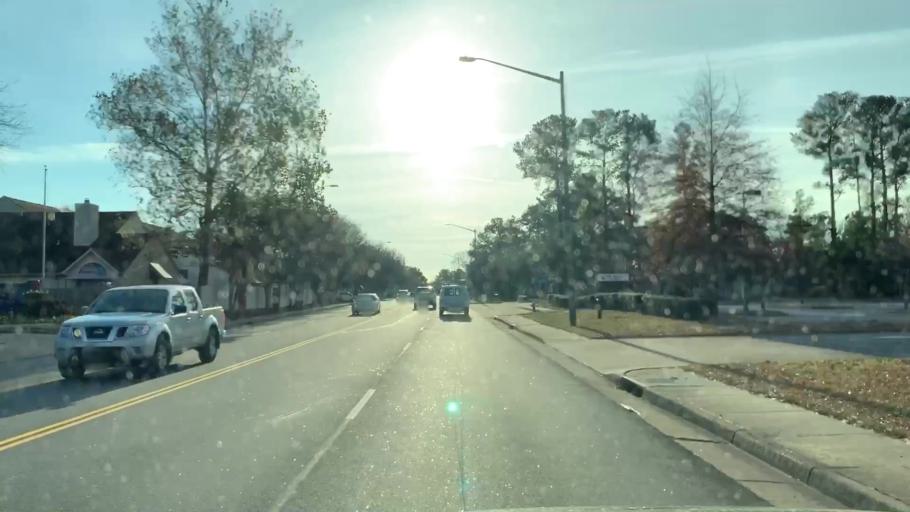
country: US
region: Virginia
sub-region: City of Chesapeake
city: Chesapeake
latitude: 36.7919
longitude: -76.1677
